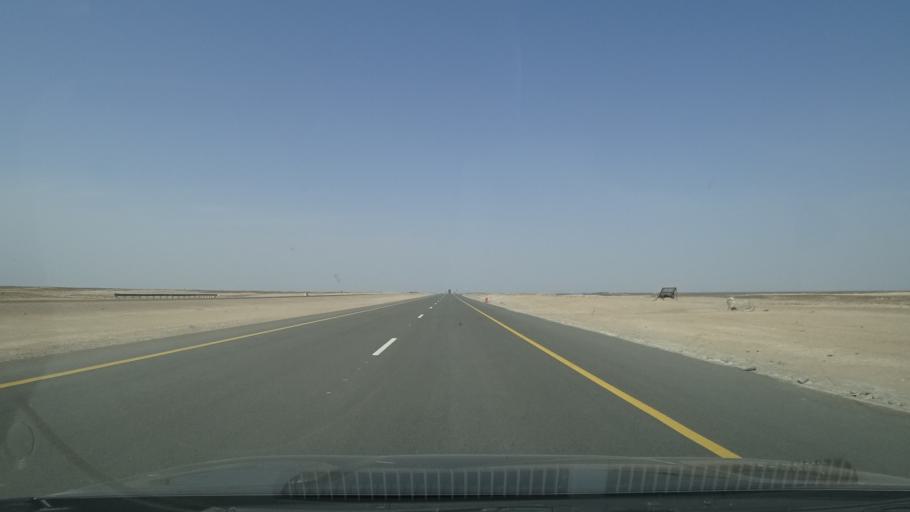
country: OM
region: Muhafazat ad Dakhiliyah
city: Adam
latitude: 21.8182
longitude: 57.3641
